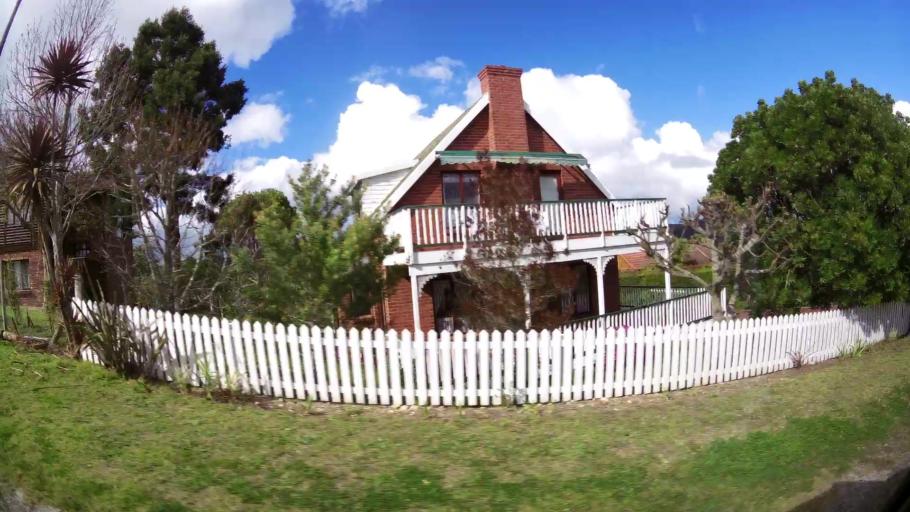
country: ZA
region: Western Cape
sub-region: Eden District Municipality
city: Knysna
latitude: -34.0533
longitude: 23.0844
